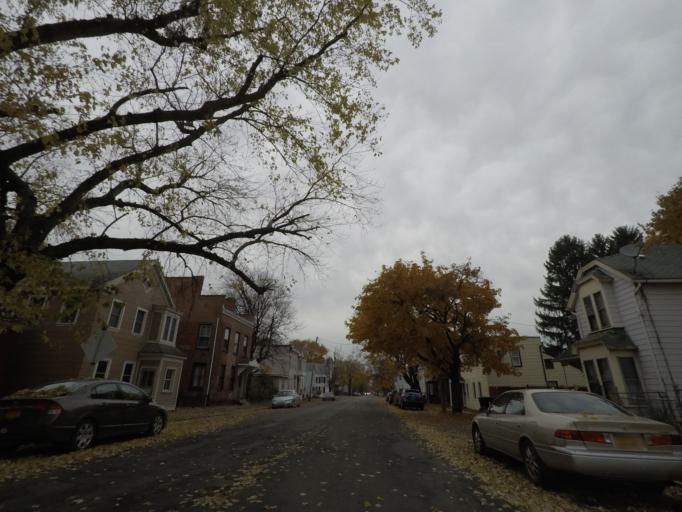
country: US
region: New York
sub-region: Saratoga County
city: Waterford
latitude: 42.7711
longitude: -73.6775
